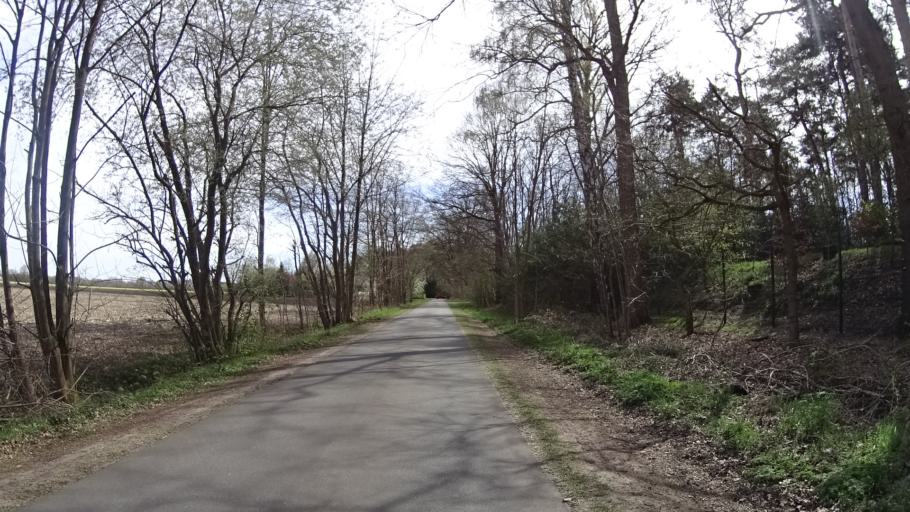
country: DE
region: Lower Saxony
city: Spelle
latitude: 52.3718
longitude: 7.4117
